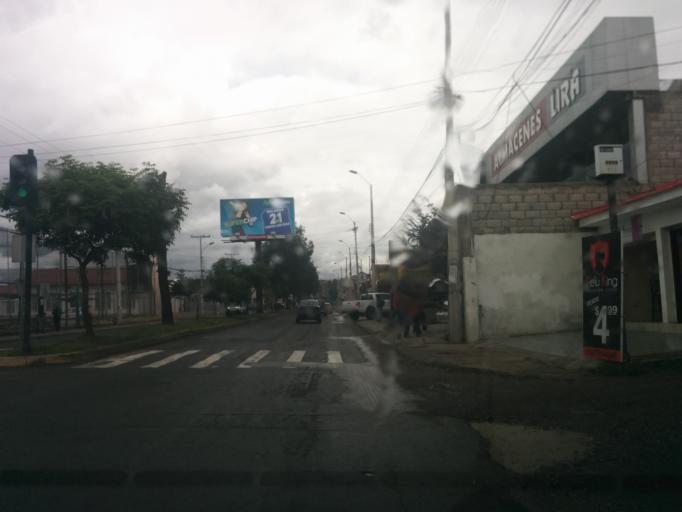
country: EC
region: Azuay
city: Cuenca
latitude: -2.8981
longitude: -78.9818
